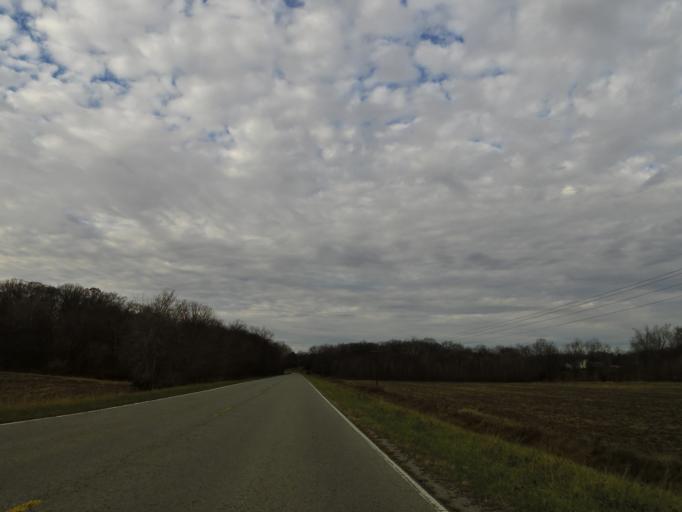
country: US
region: Illinois
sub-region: Jefferson County
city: Mount Vernon
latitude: 38.3791
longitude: -89.0281
